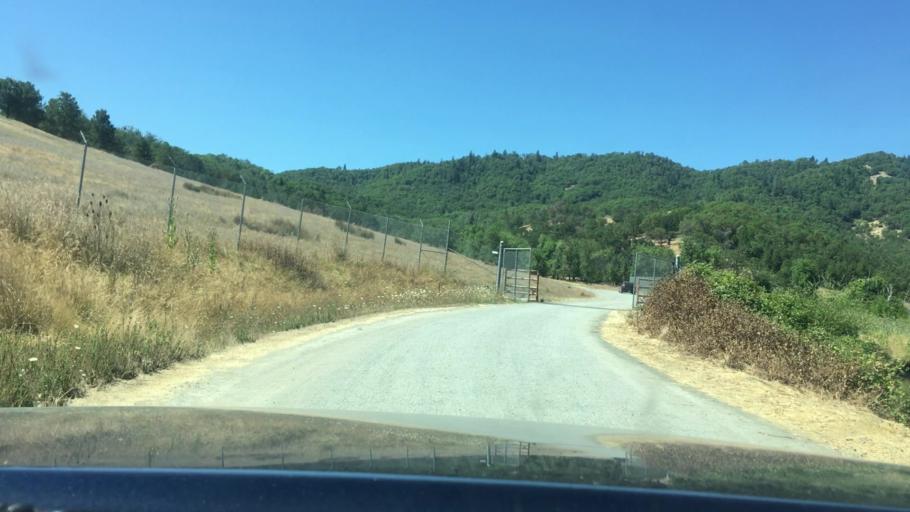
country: US
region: Oregon
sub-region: Douglas County
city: Winston
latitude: 43.1297
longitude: -123.4345
